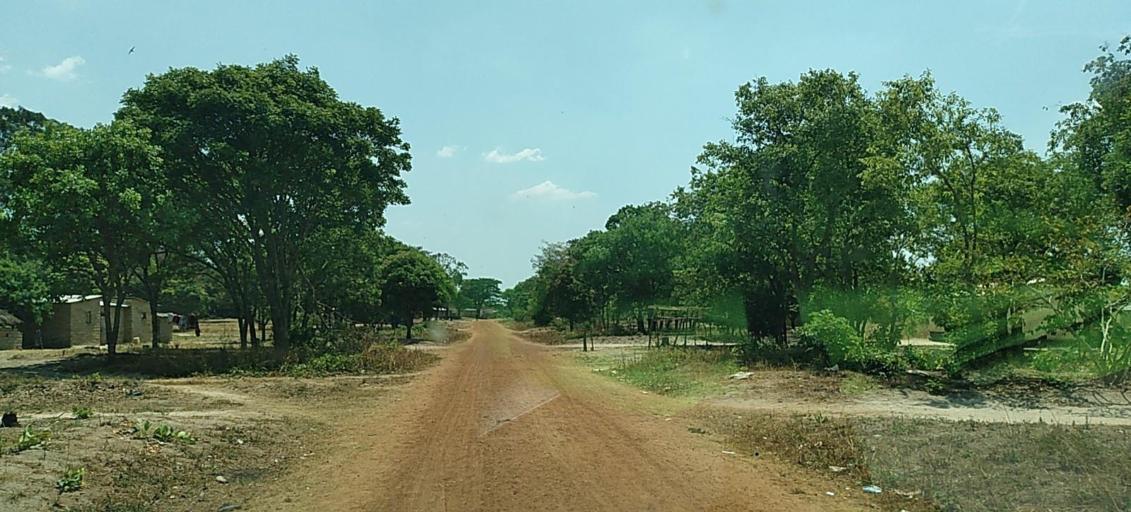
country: CD
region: Katanga
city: Kolwezi
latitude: -11.2974
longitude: 25.2140
